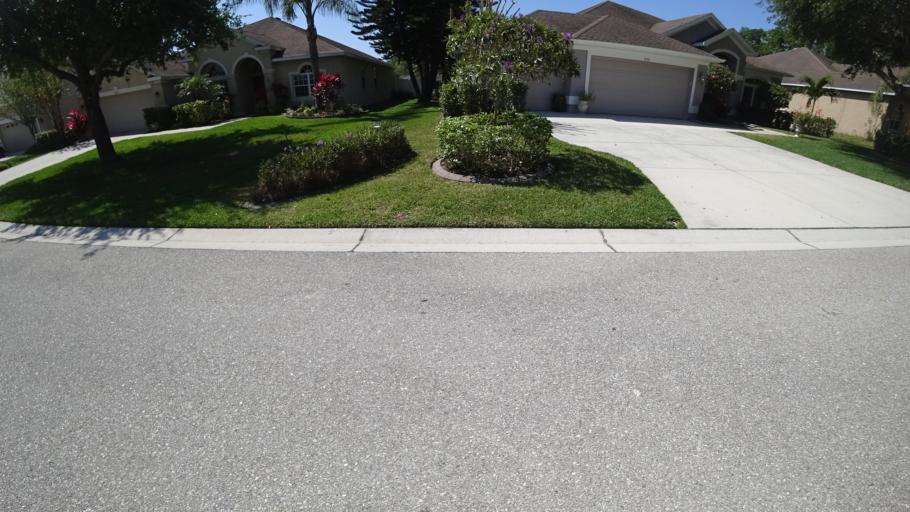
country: US
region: Florida
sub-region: Manatee County
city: Samoset
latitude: 27.4650
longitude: -82.5226
